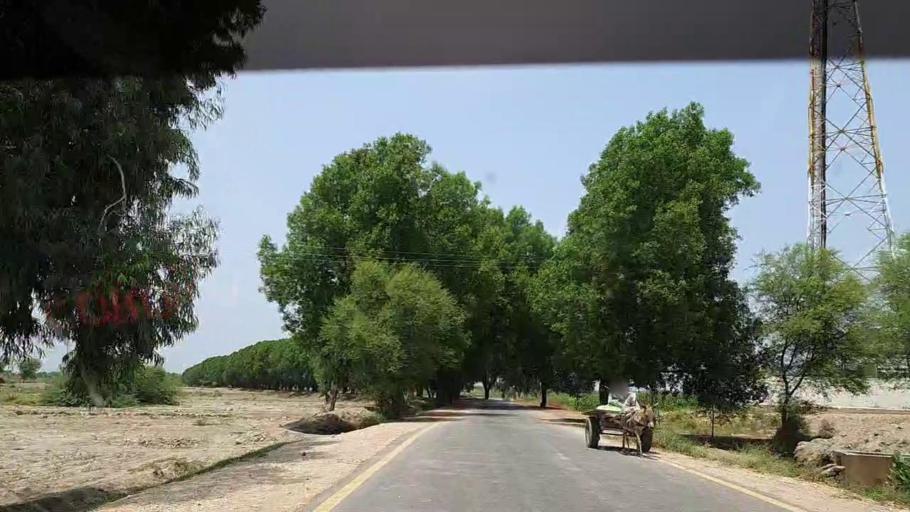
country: PK
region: Sindh
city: Adilpur
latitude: 27.8747
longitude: 69.2765
